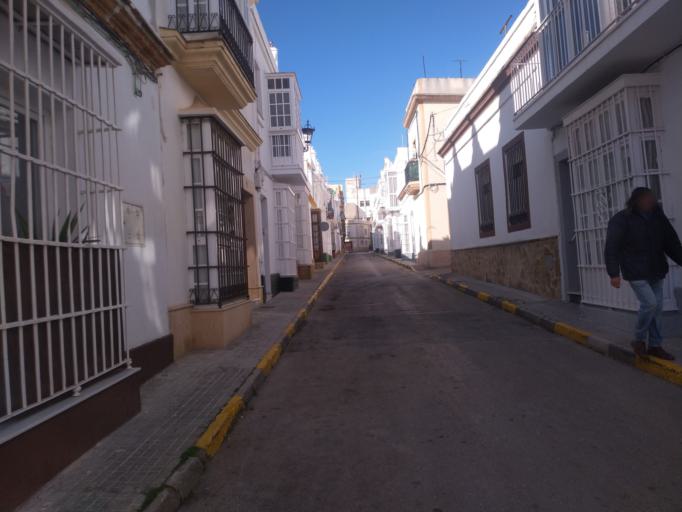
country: ES
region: Andalusia
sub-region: Provincia de Cadiz
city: San Fernando
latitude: 36.4646
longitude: -6.1949
